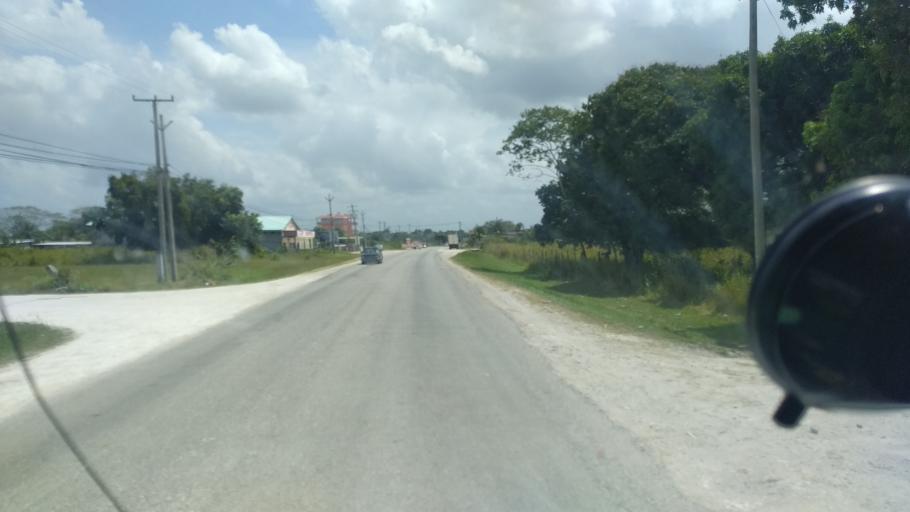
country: BZ
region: Orange Walk
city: Orange Walk
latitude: 18.0591
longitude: -88.5691
